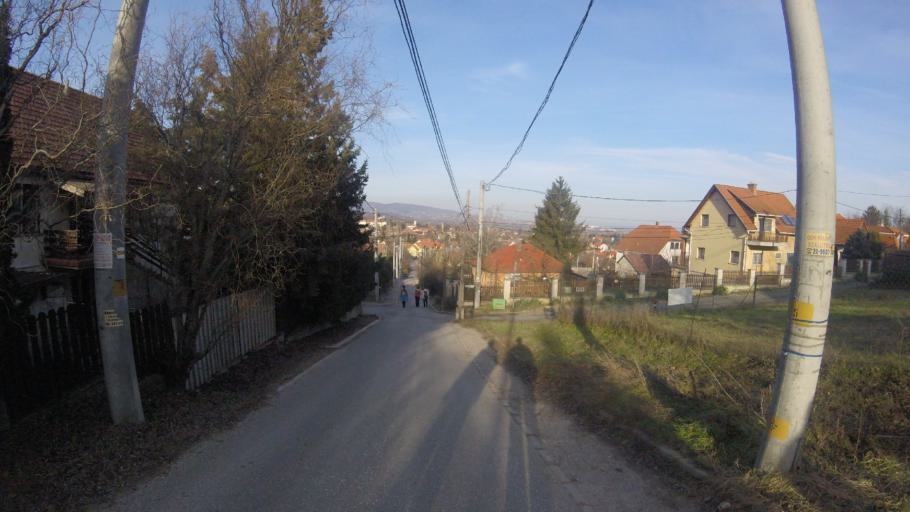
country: HU
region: Pest
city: Nagykovacsi
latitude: 47.6438
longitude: 19.0146
